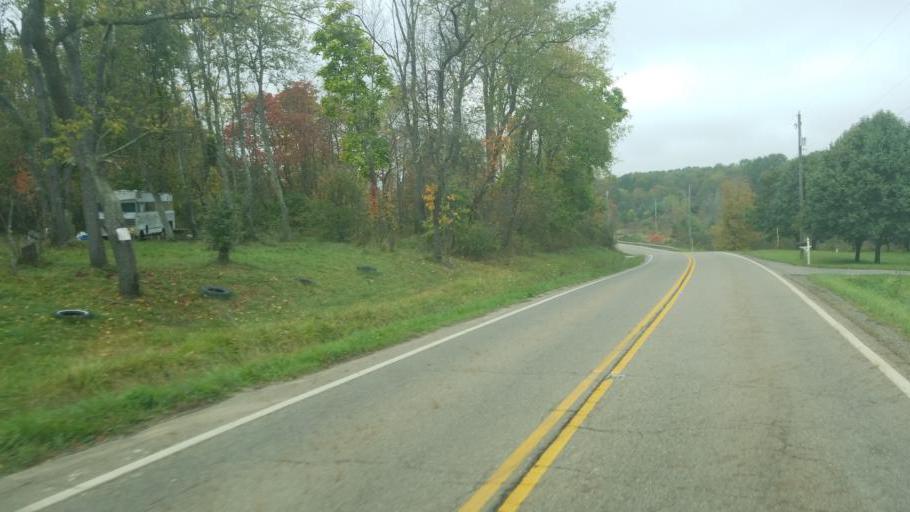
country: US
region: Ohio
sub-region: Carroll County
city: Lake Mohawk
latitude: 40.6319
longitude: -81.2902
